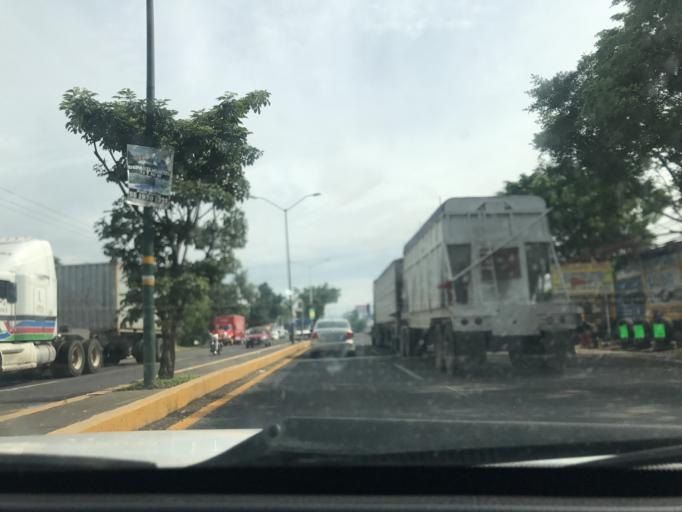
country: MX
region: Morelos
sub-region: Cuautla
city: Tierra Larga (Campo Nuevo)
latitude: 18.8757
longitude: -98.9231
